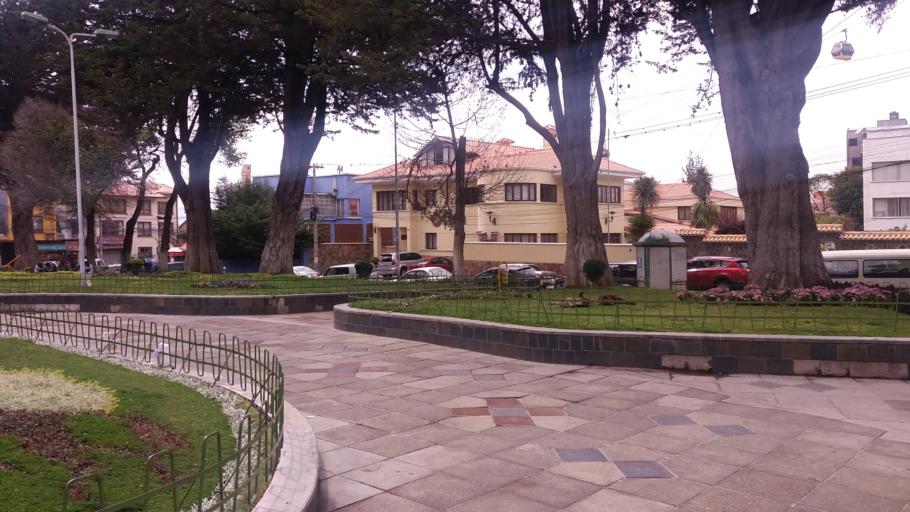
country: BO
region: La Paz
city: La Paz
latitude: -16.5144
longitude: -68.1286
